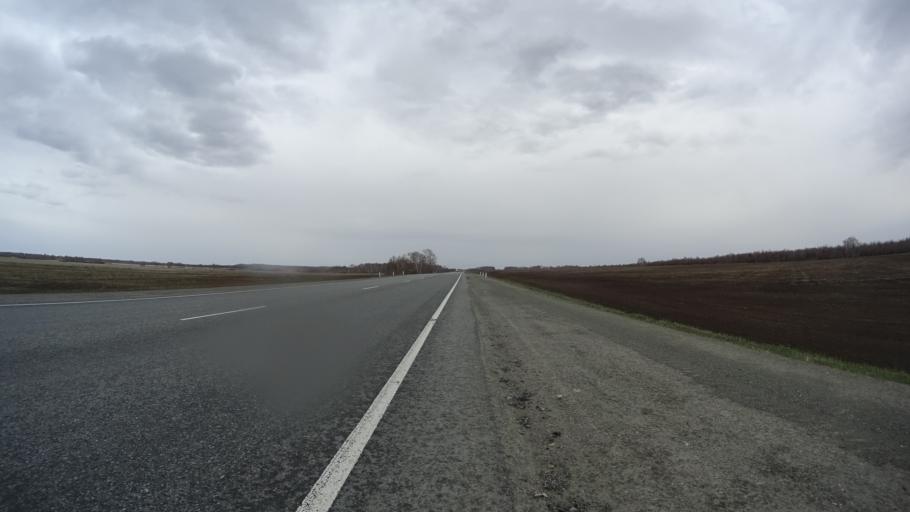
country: RU
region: Chelyabinsk
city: Krasnogorskiy
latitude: 54.6669
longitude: 61.2522
